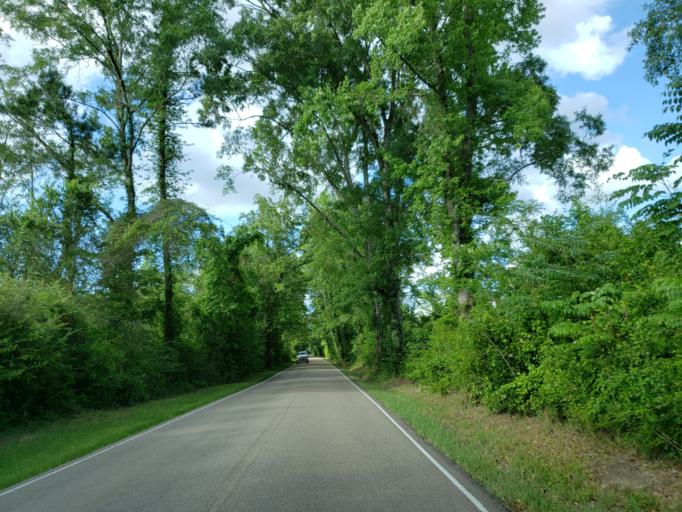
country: US
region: Mississippi
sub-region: Forrest County
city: Hattiesburg
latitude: 31.2513
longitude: -89.2402
